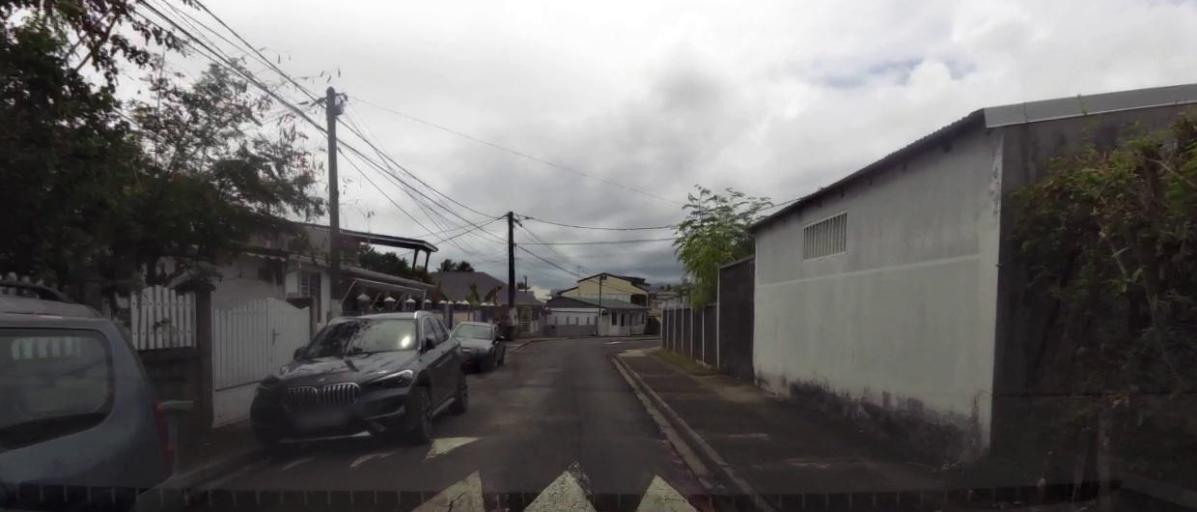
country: GP
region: Guadeloupe
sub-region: Guadeloupe
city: Petit-Bourg
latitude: 16.1965
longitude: -61.5905
